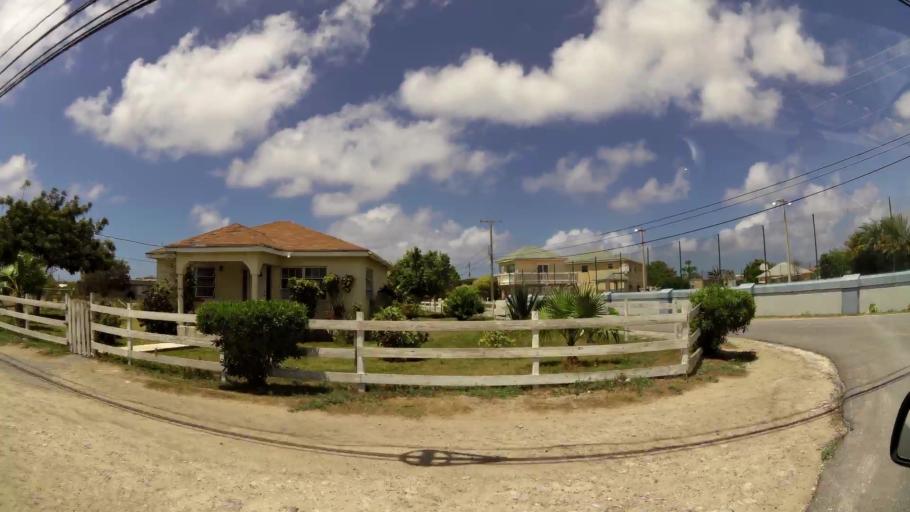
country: TC
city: Cockburn Town
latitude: 21.4623
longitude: -71.1394
